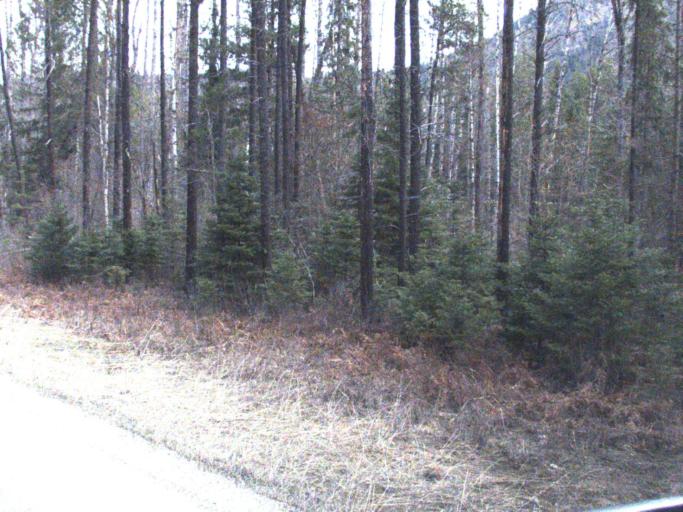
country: US
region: Washington
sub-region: Stevens County
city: Chewelah
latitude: 48.5895
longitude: -117.3525
